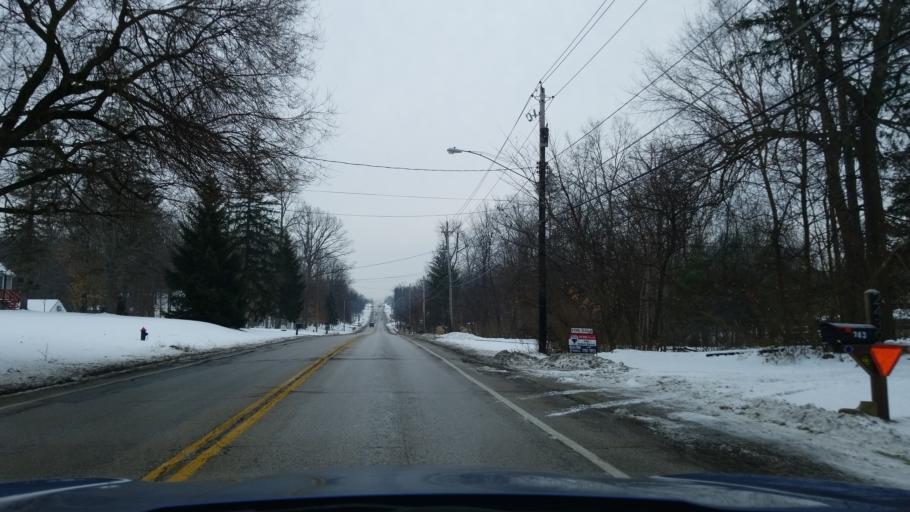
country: US
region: Ohio
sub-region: Cuyahoga County
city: Broadview Heights
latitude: 41.3138
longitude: -81.6996
